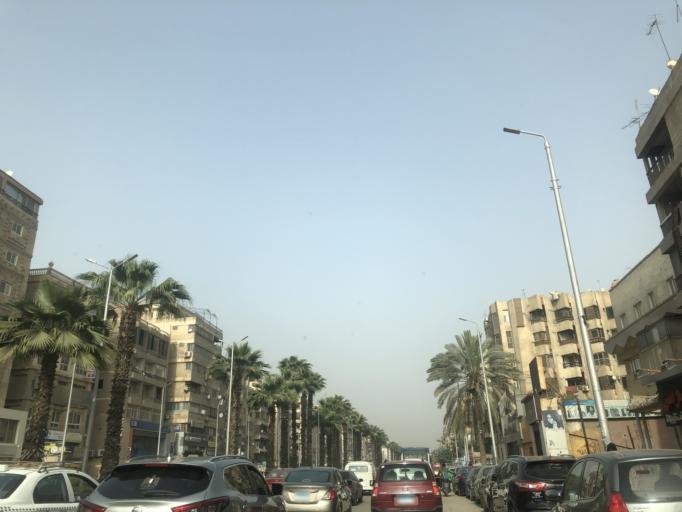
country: EG
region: Al Jizah
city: Al Jizah
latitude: 29.9926
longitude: 31.1568
